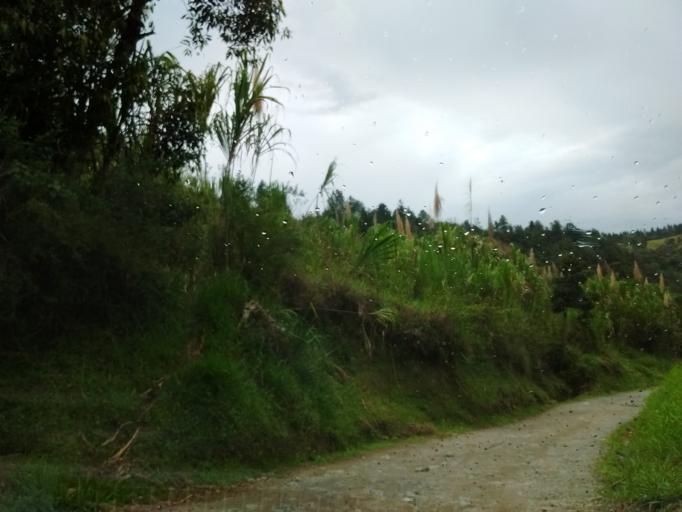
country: CO
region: Cauca
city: Cajibio
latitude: 2.5618
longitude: -76.6341
